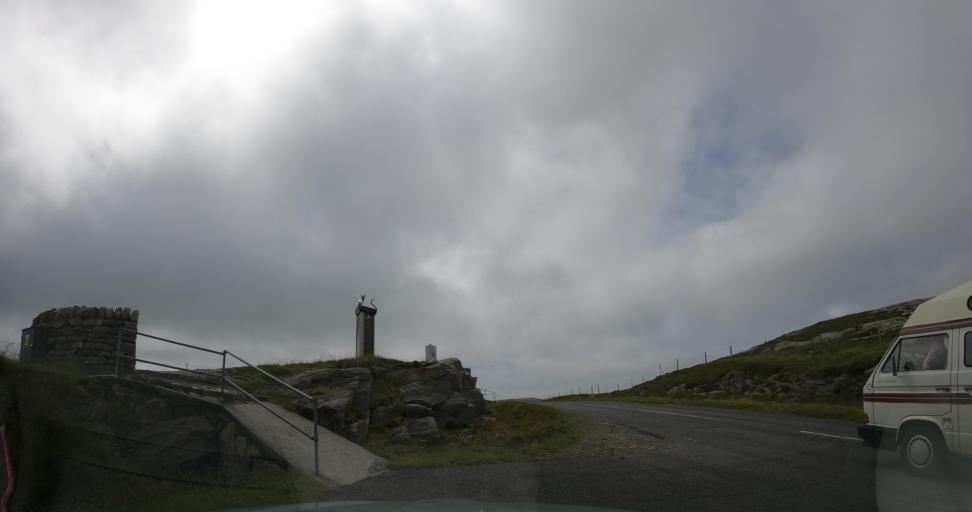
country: GB
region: Scotland
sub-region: Eilean Siar
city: Barra
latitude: 56.9503
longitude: -7.5105
